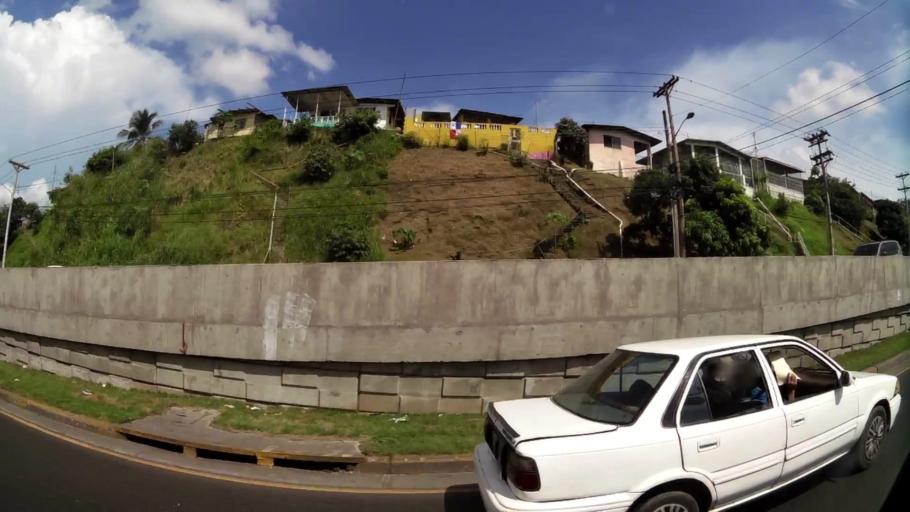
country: PA
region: Panama
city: San Miguelito
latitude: 9.0289
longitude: -79.4947
